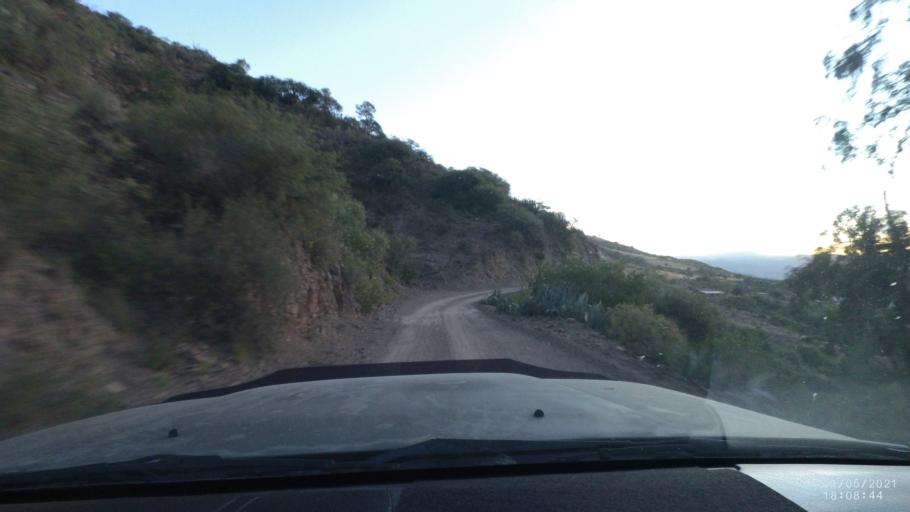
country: BO
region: Cochabamba
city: Capinota
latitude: -17.6860
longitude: -66.1912
